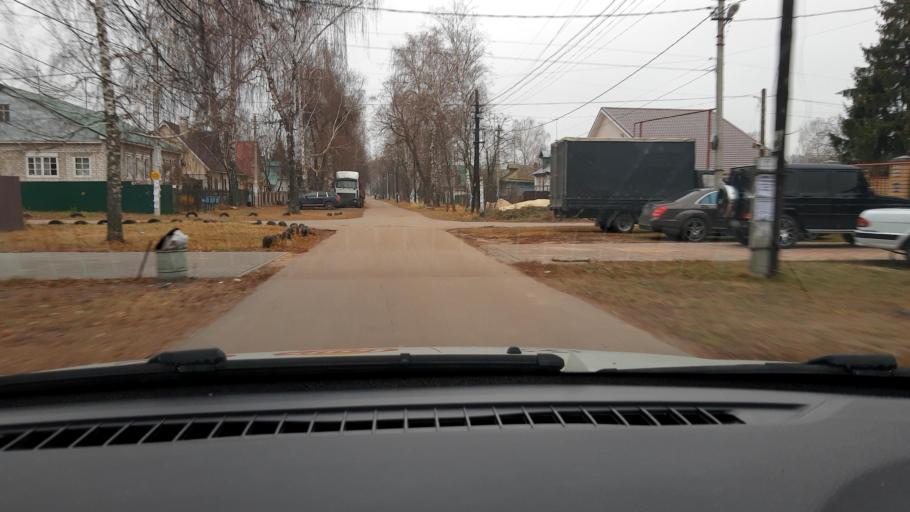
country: RU
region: Nizjnij Novgorod
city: Gorbatovka
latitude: 56.2042
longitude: 43.7671
